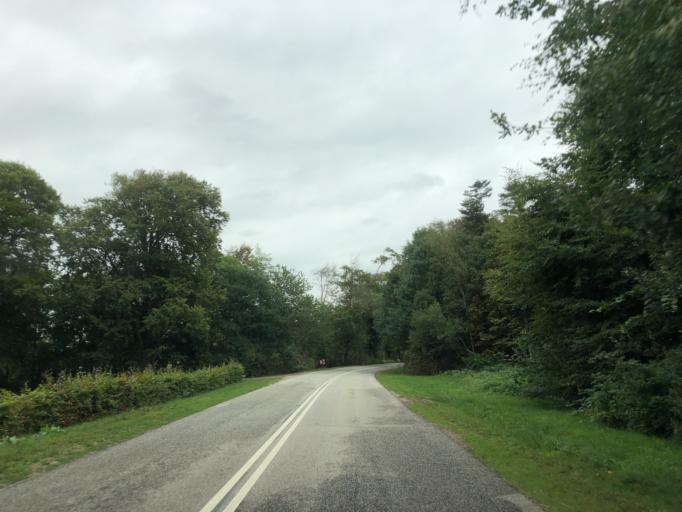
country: DK
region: Central Jutland
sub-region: Herning Kommune
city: Snejbjerg
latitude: 56.1691
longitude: 8.8605
